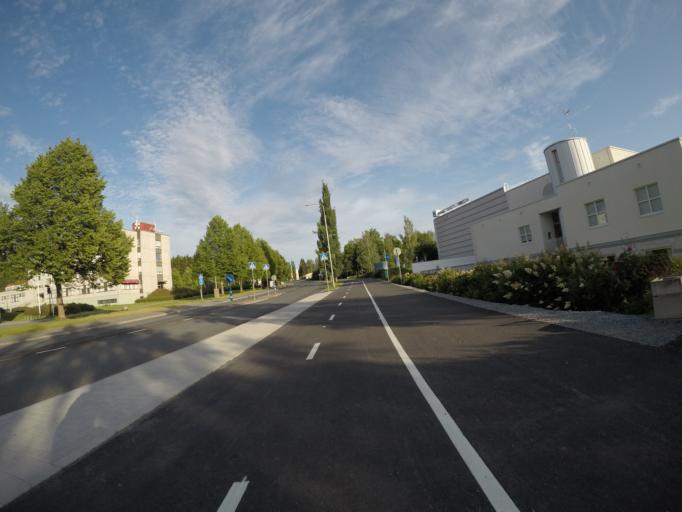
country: FI
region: Haeme
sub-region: Haemeenlinna
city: Haemeenlinna
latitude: 60.9865
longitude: 24.4404
